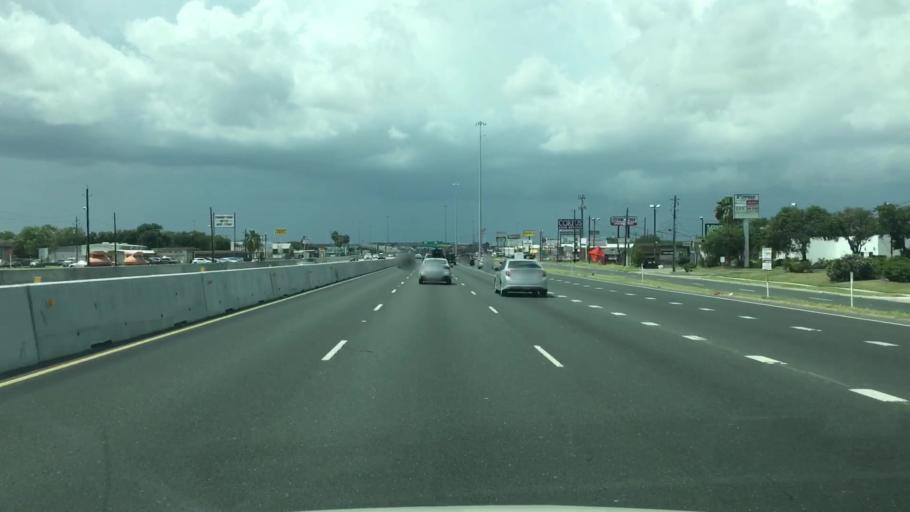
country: US
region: Texas
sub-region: Nueces County
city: Corpus Christi
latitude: 27.7314
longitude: -97.4184
